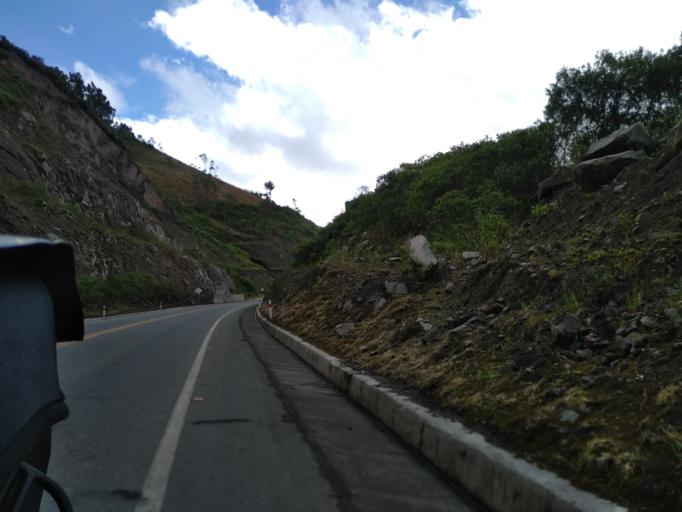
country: EC
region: Tungurahua
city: Banos
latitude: -1.4790
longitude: -78.5185
